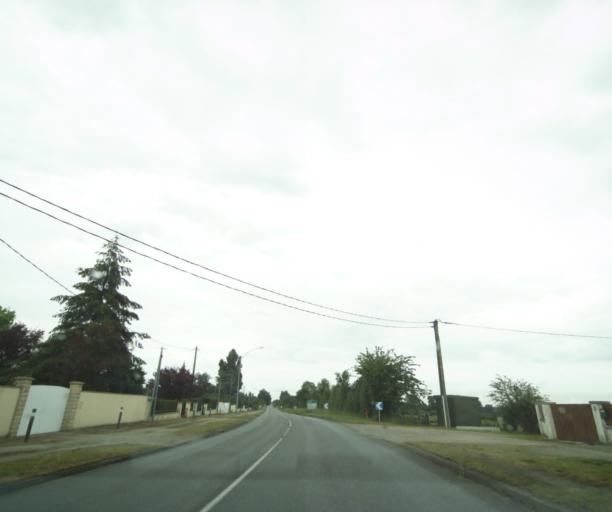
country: FR
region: Poitou-Charentes
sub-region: Departement des Deux-Sevres
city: Viennay
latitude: 46.6731
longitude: -0.2451
